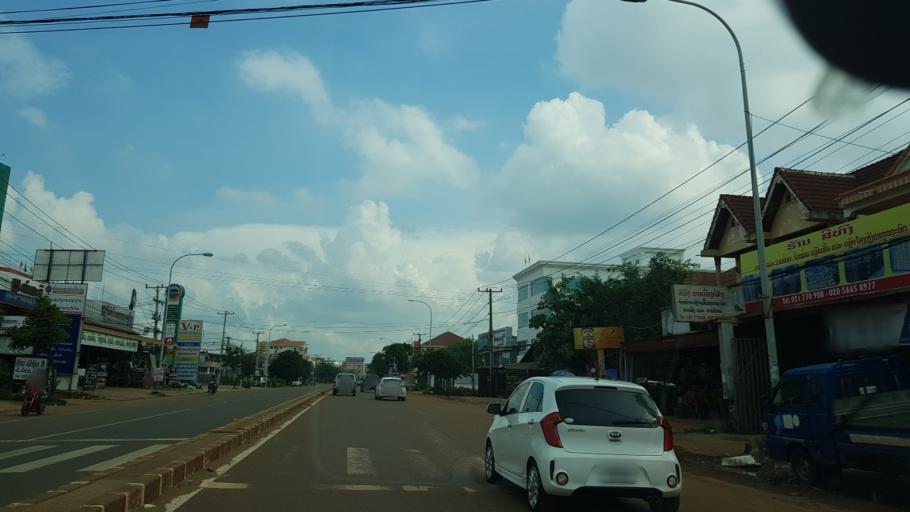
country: LA
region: Vientiane
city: Vientiane
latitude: 18.0259
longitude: 102.6516
